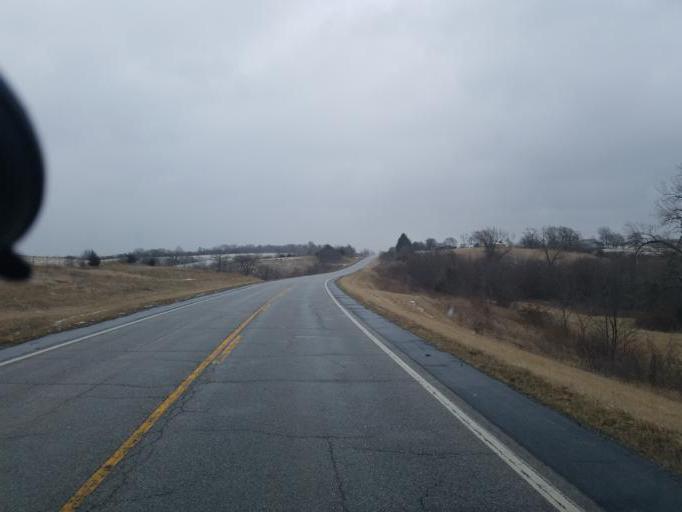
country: US
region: Missouri
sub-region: Putnam County
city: Unionville
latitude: 40.4718
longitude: -92.9361
